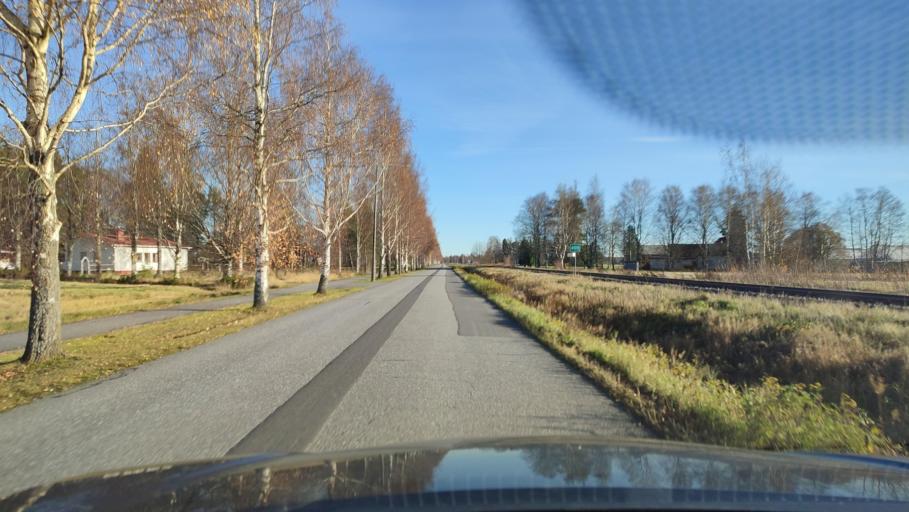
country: FI
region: Southern Ostrobothnia
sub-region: Suupohja
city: Teuva
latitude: 62.4697
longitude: 21.7139
